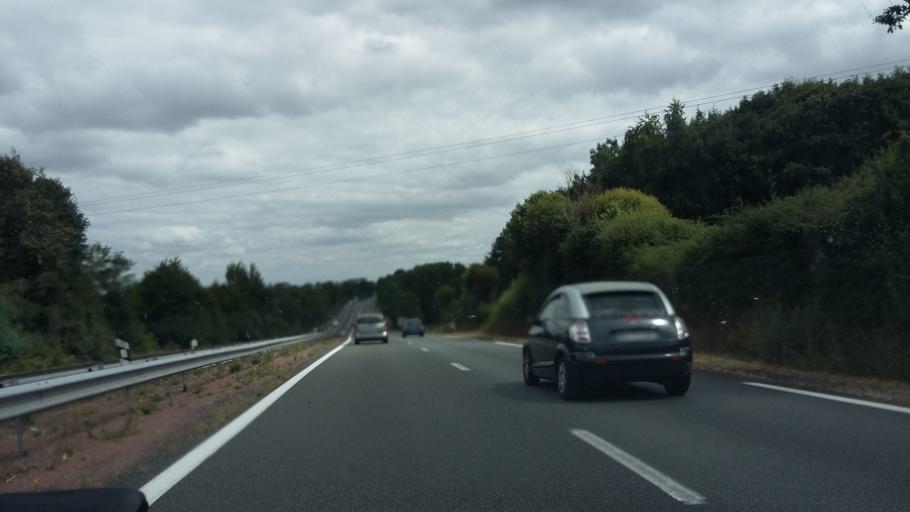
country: FR
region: Pays de la Loire
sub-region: Departement de la Vendee
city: Mouilleron-le-Captif
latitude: 46.6895
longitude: -1.4641
